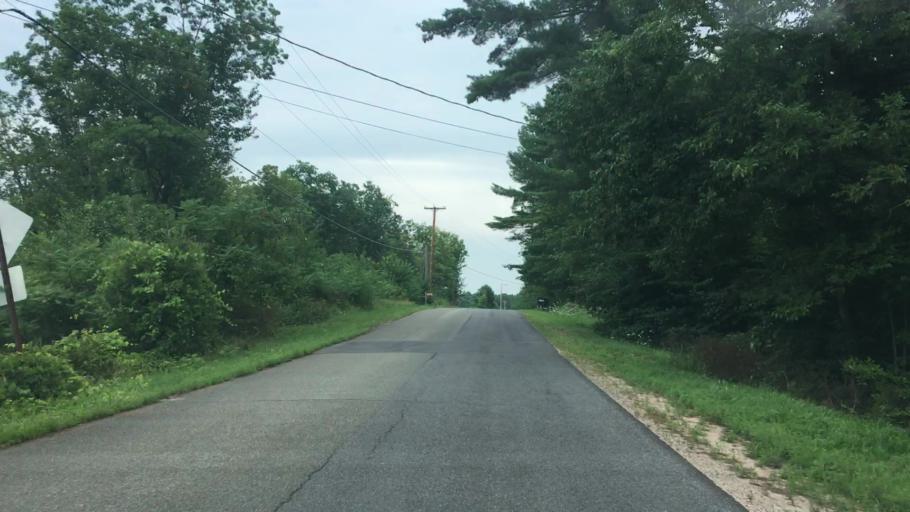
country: US
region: New York
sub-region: Clinton County
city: Peru
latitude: 44.6037
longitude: -73.6108
